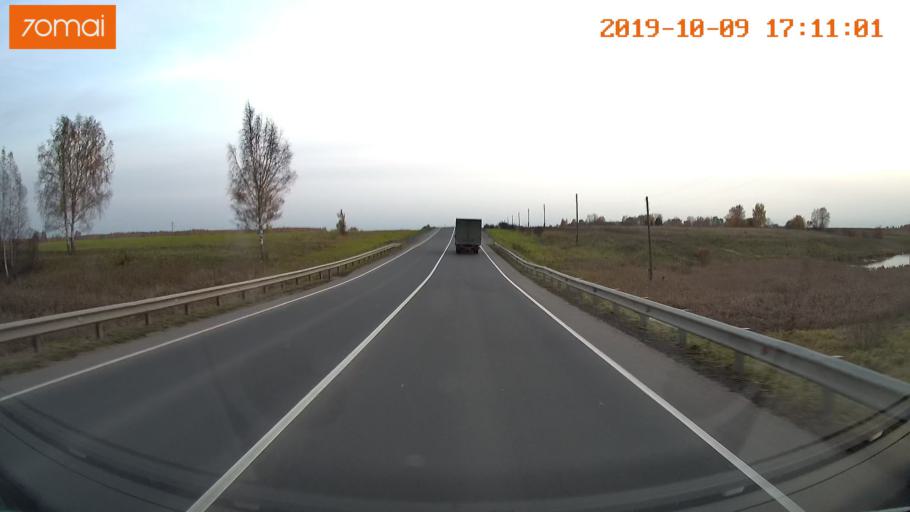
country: RU
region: Ivanovo
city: Privolzhsk
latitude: 57.3480
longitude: 41.2530
